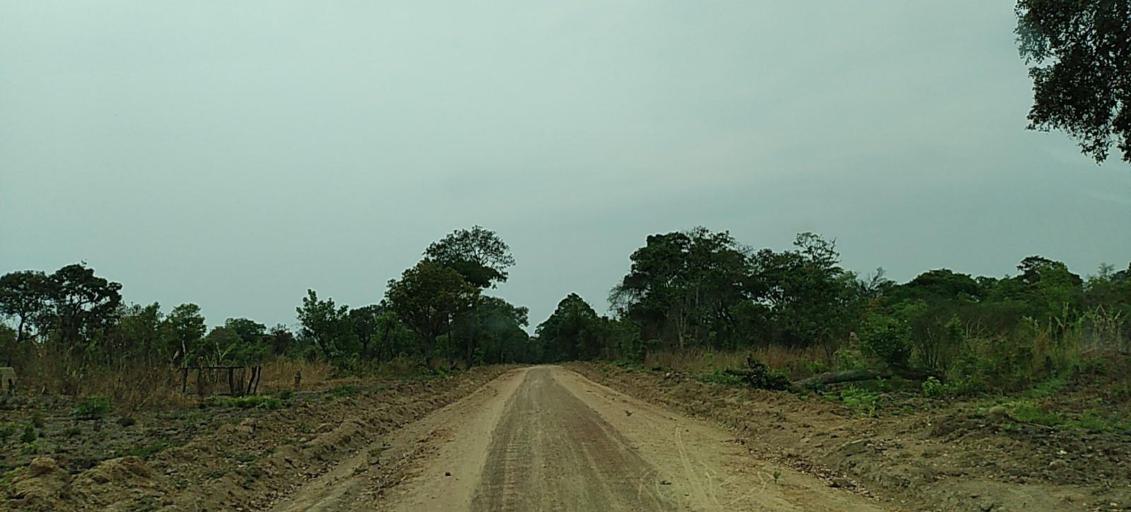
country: ZM
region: North-Western
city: Solwezi
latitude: -12.5168
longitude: 26.5259
